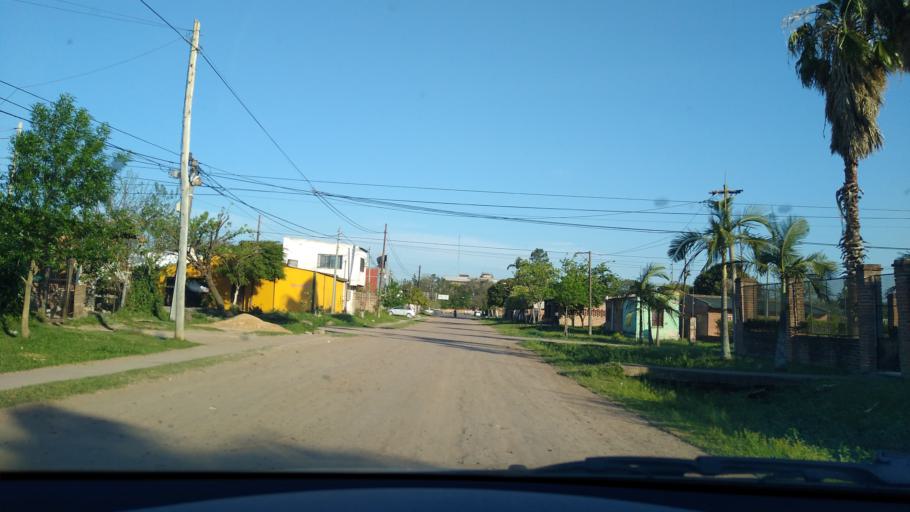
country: AR
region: Chaco
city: Barranqueras
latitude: -27.4883
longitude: -58.9320
